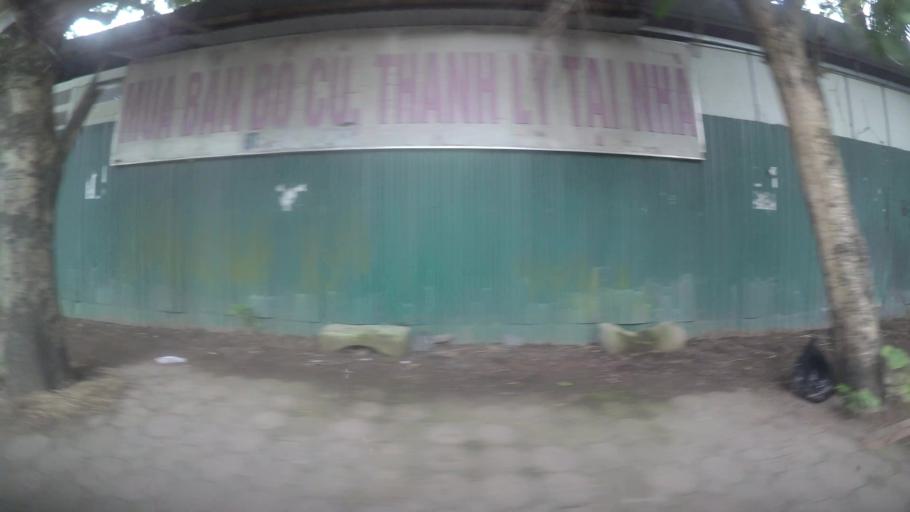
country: VN
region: Ha Noi
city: Tay Ho
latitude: 21.0750
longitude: 105.8156
